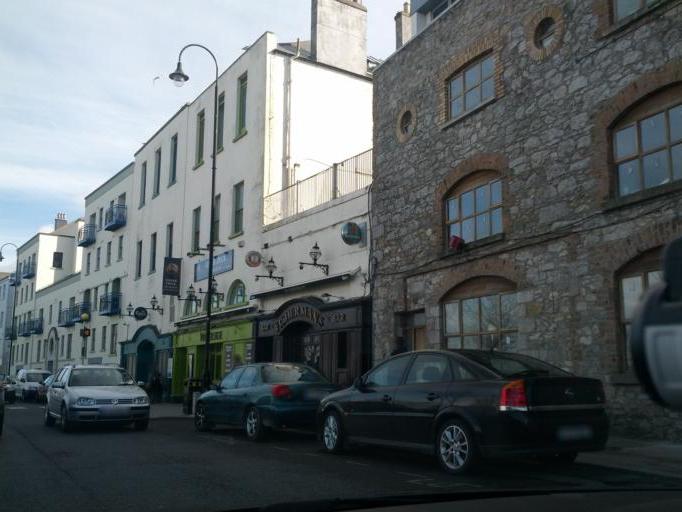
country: IE
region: Leinster
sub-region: Fingal County
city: Howth
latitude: 53.3880
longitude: -6.0691
